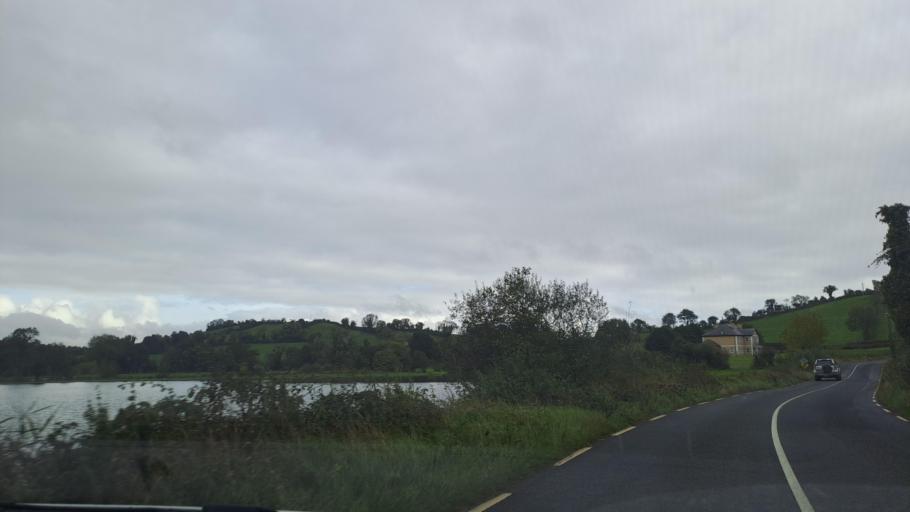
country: IE
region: Ulster
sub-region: An Cabhan
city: Cootehill
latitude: 54.0400
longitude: -7.0453
